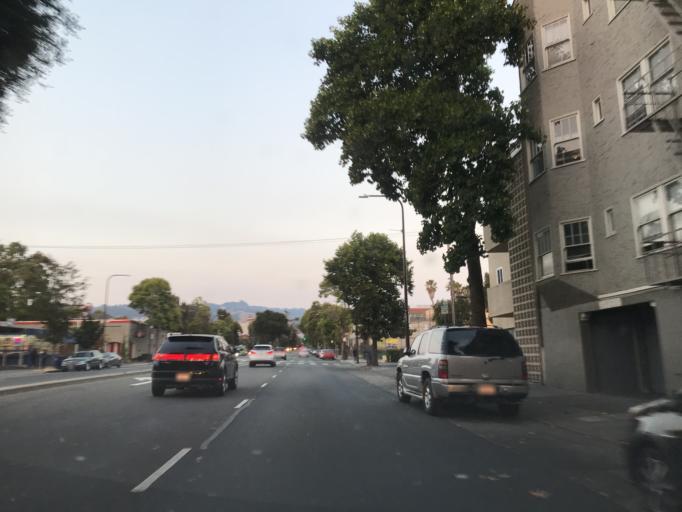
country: US
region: California
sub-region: Alameda County
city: Berkeley
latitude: 37.8692
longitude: -122.2903
